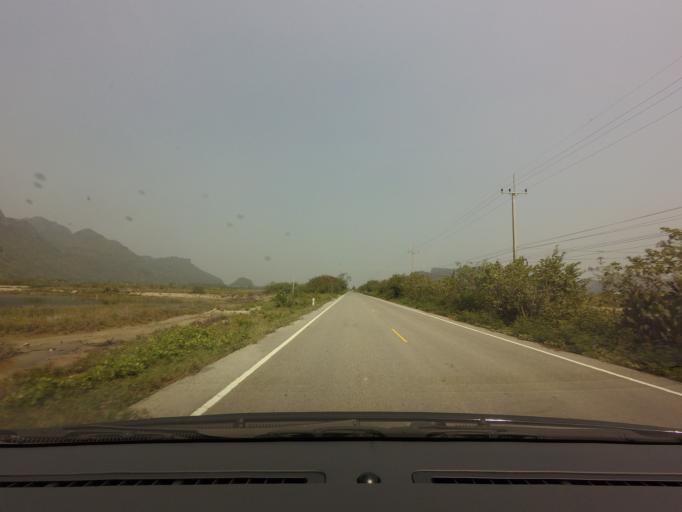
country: TH
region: Prachuap Khiri Khan
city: Sam Roi Yot
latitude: 12.1903
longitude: 99.9776
